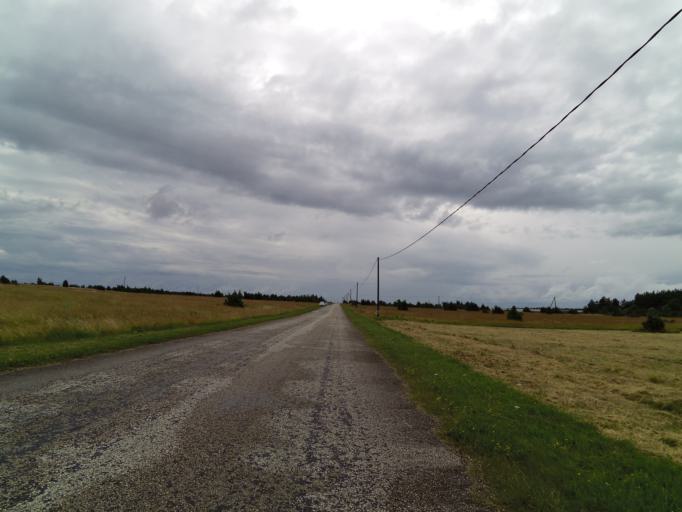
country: EE
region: Laeaene
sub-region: Vormsi vald
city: Hullo
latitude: 58.9775
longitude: 23.3093
